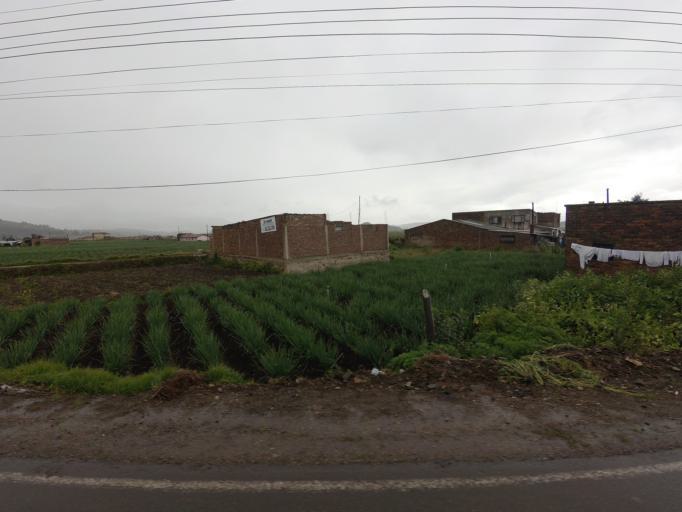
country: CO
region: Boyaca
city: Aquitania
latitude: 5.5287
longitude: -72.8839
